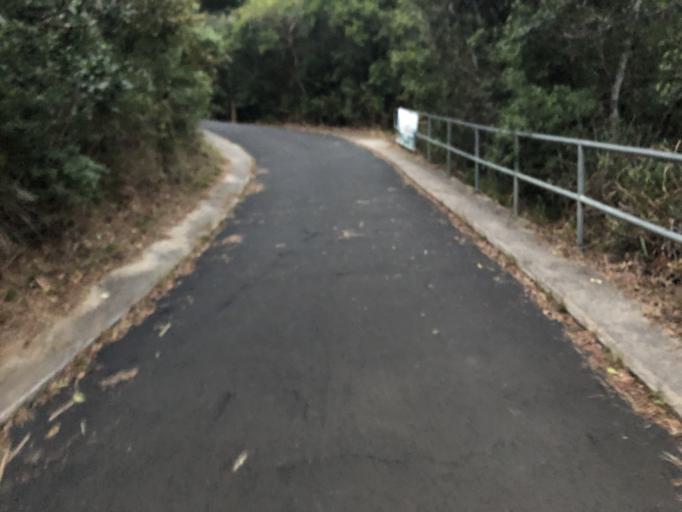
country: HK
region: Wanchai
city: Wan Chai
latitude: 22.2575
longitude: 114.2088
